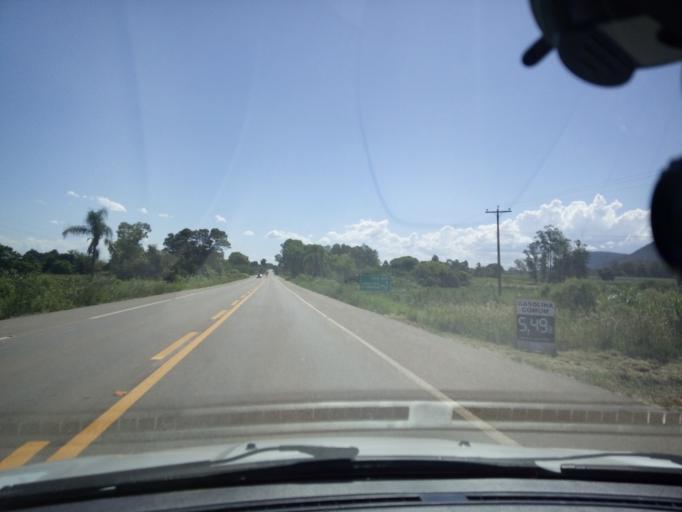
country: BR
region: Rio Grande do Sul
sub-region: Santa Maria
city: Santa Maria
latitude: -29.7330
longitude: -53.5264
